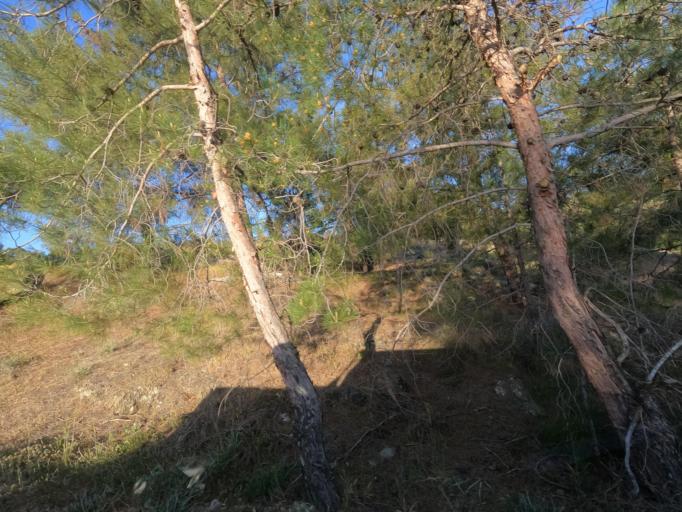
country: CY
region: Lefkosia
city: Peristerona
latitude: 35.0662
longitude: 33.0437
